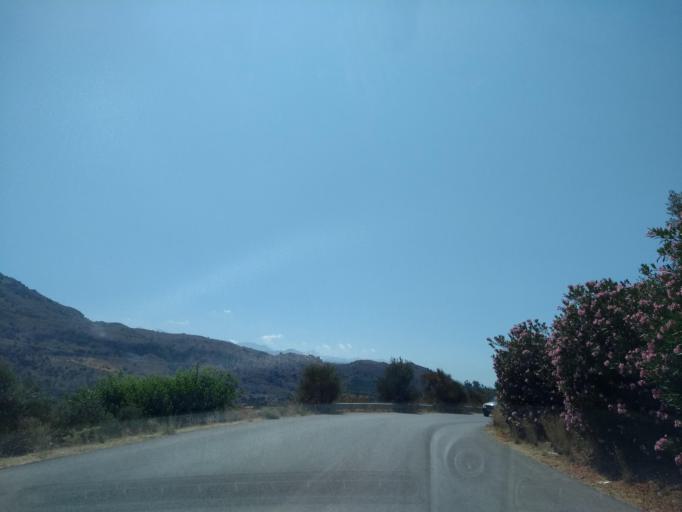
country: GR
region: Crete
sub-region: Nomos Chanias
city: Georgioupolis
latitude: 35.3572
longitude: 24.2642
